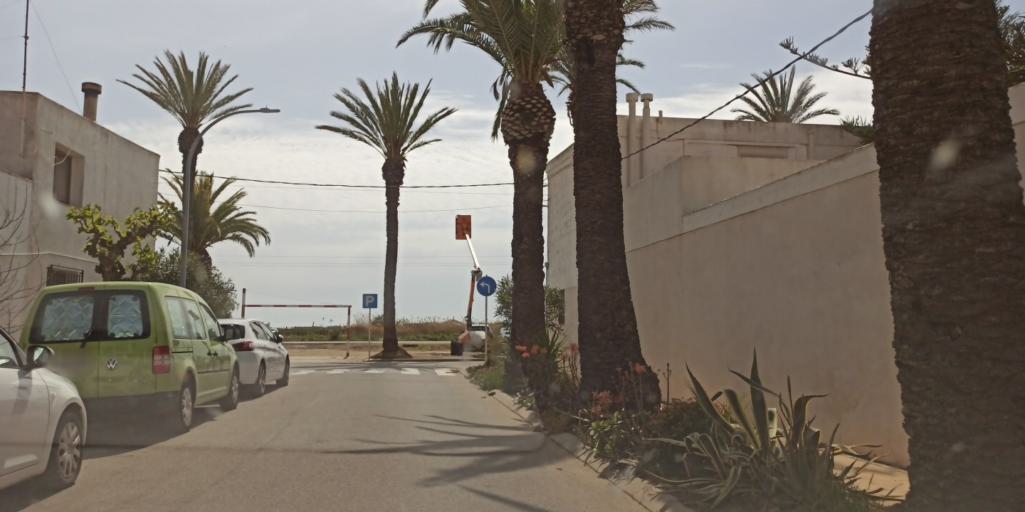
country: ES
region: Catalonia
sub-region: Provincia de Tarragona
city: Deltebre
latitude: 40.6448
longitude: 0.6872
